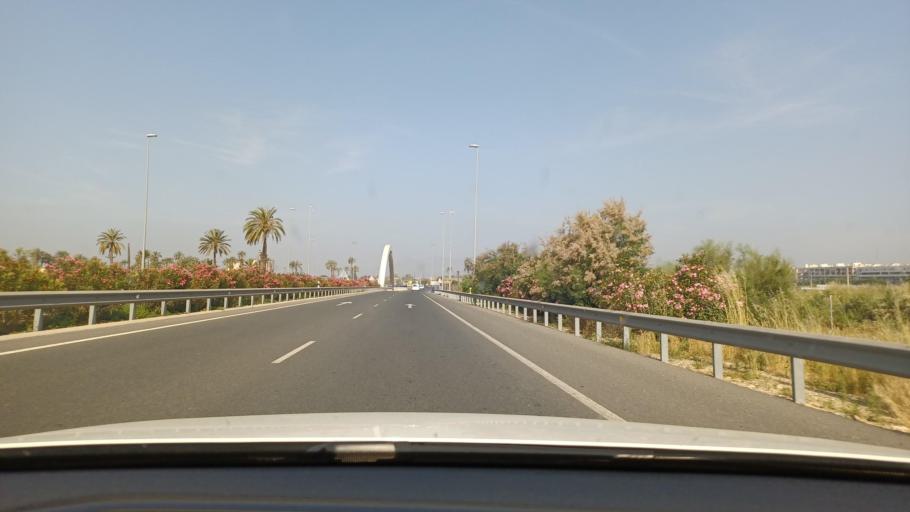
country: ES
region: Valencia
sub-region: Provincia de Alicante
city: Elche
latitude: 38.2496
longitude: -0.6996
